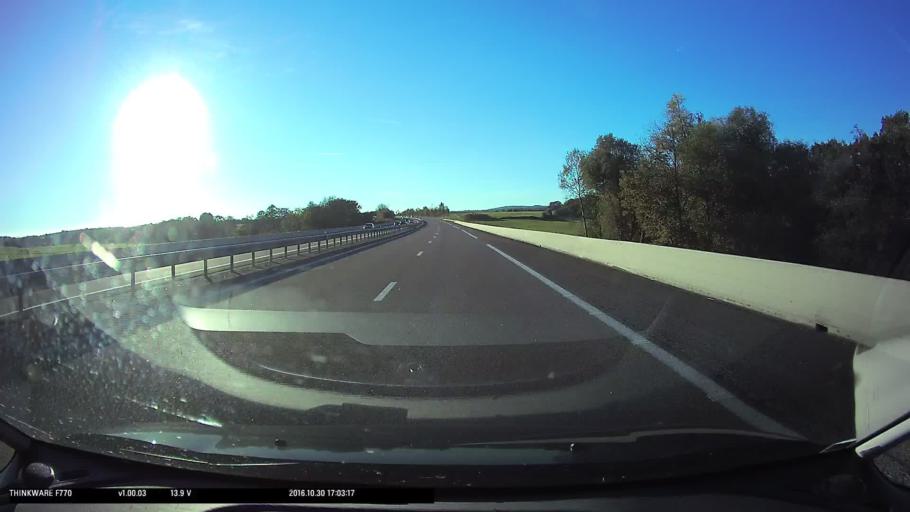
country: FR
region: Franche-Comte
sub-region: Departement du Jura
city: Orchamps
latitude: 47.1659
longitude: 5.6329
